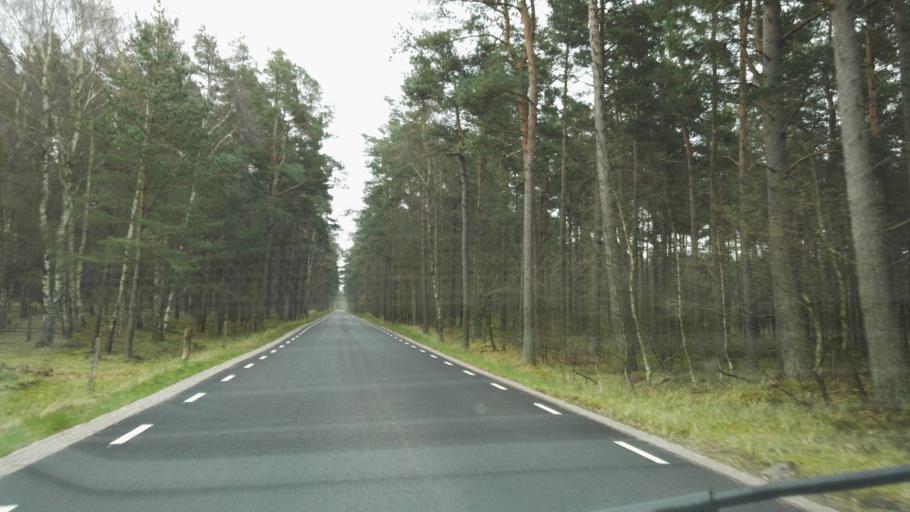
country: SE
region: Skane
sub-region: Simrishamns Kommun
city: Simrishamn
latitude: 55.3934
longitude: 14.1813
